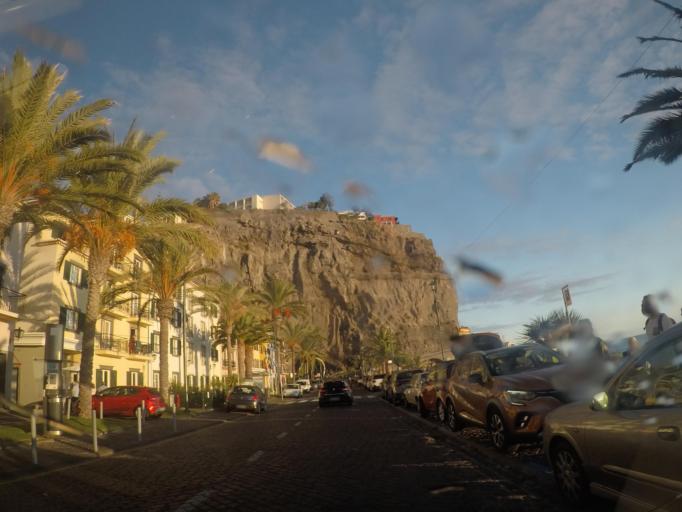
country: PT
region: Madeira
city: Ponta do Sol
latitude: 32.6799
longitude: -17.1052
